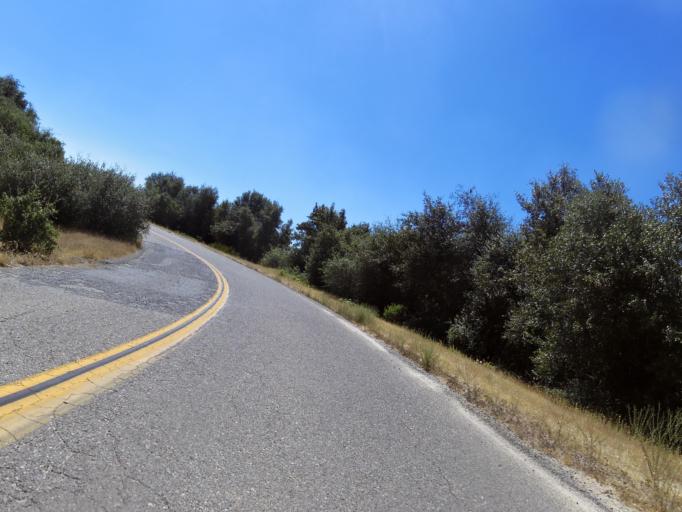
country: US
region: California
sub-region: Madera County
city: Ahwahnee
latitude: 37.3600
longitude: -119.6962
